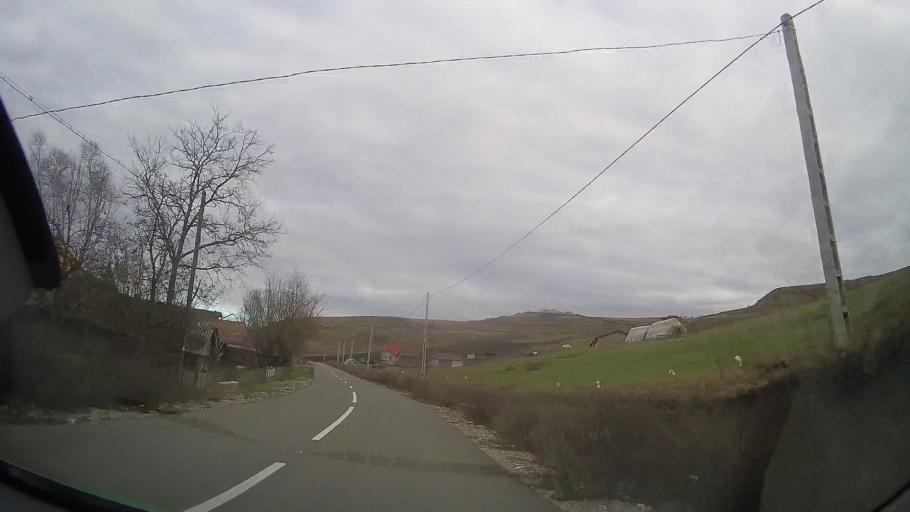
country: RO
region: Bistrita-Nasaud
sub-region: Comuna Silvasu de Campie
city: Silvasu de Campie
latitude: 46.8131
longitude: 24.2964
